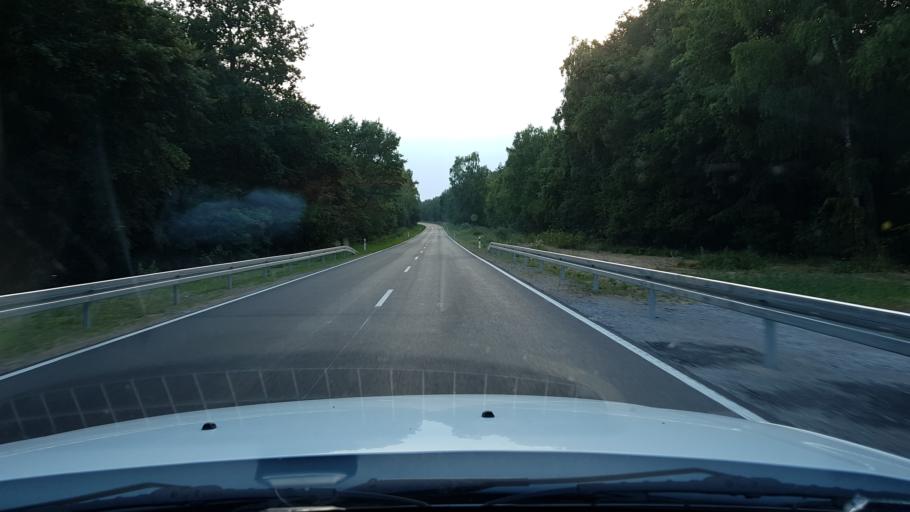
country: PL
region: West Pomeranian Voivodeship
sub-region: Powiat goleniowski
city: Maszewo
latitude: 53.4312
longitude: 15.0171
